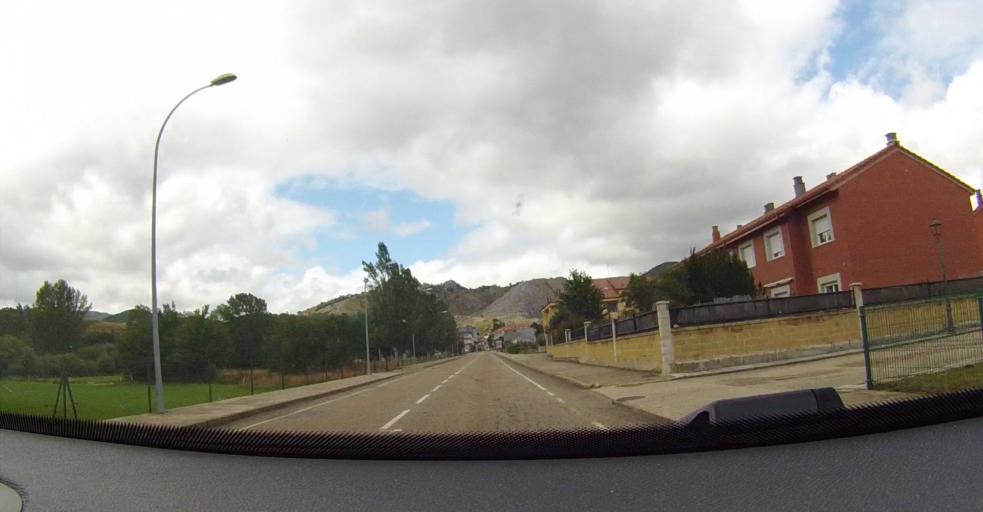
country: ES
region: Castille and Leon
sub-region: Provincia de Leon
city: Puebla de Lillo
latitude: 43.0045
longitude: -5.2692
